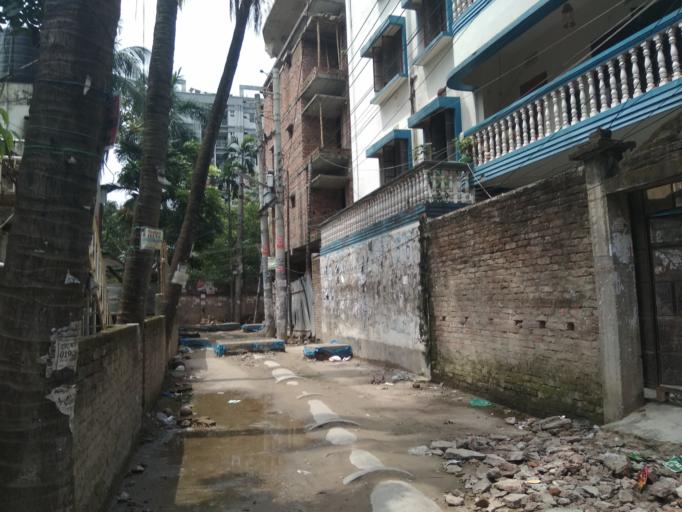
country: BD
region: Dhaka
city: Azimpur
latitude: 23.8022
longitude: 90.3667
